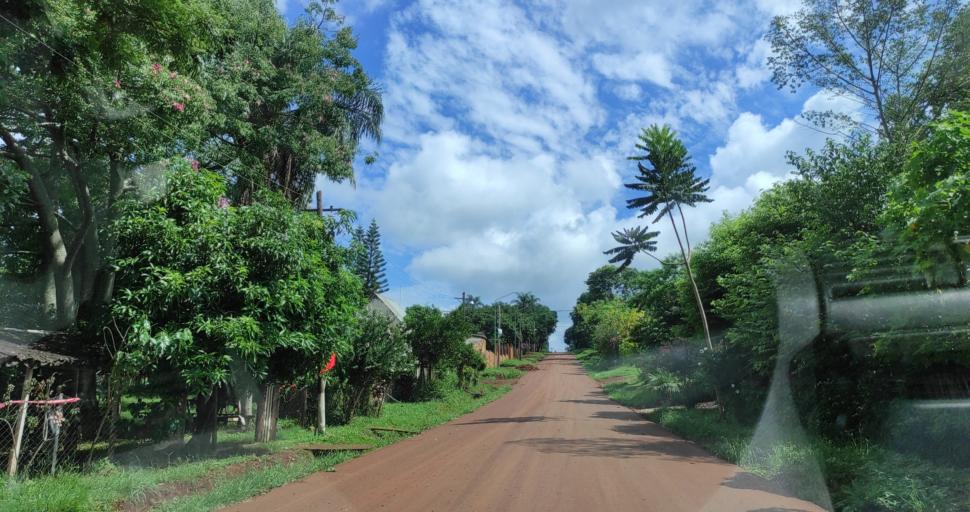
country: AR
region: Corrientes
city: San Carlos
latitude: -27.7513
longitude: -55.8911
